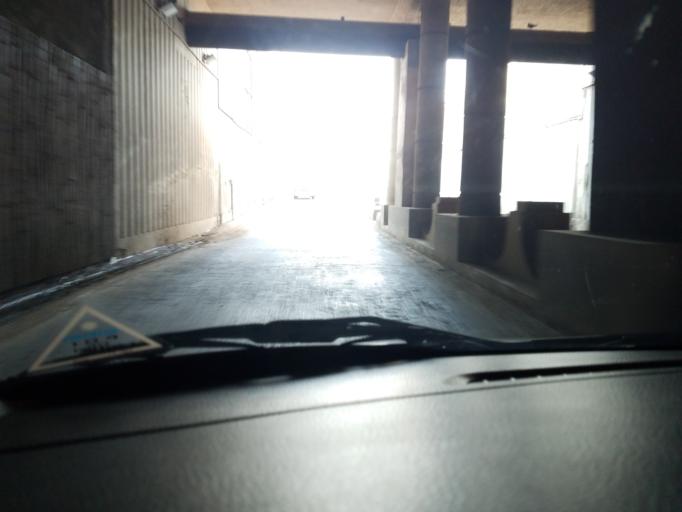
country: PK
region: Sindh
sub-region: Karachi District
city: Karachi
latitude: 24.8524
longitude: 67.0342
